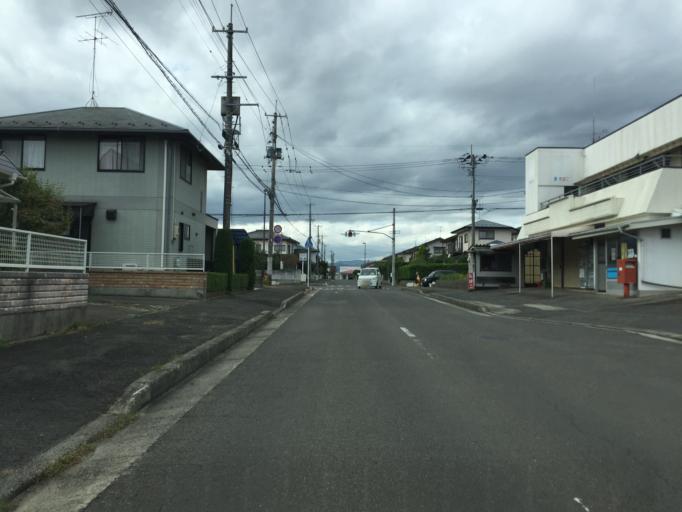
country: JP
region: Fukushima
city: Fukushima-shi
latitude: 37.7076
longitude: 140.4736
